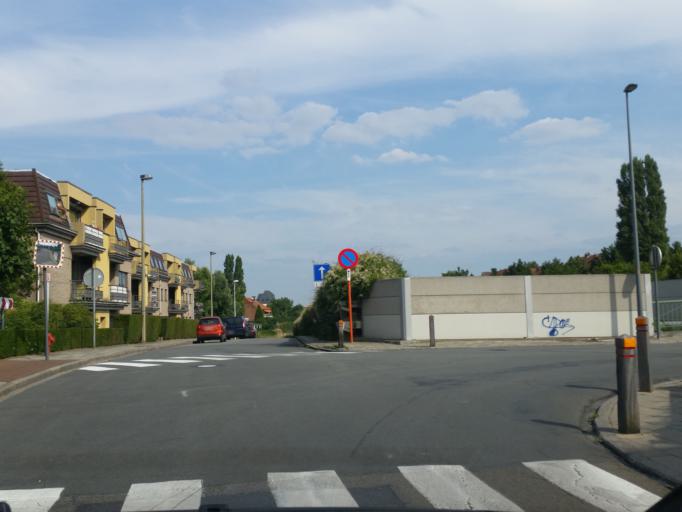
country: BE
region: Flanders
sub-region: Provincie Vlaams-Brabant
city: Diegem
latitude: 50.8919
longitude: 4.4358
